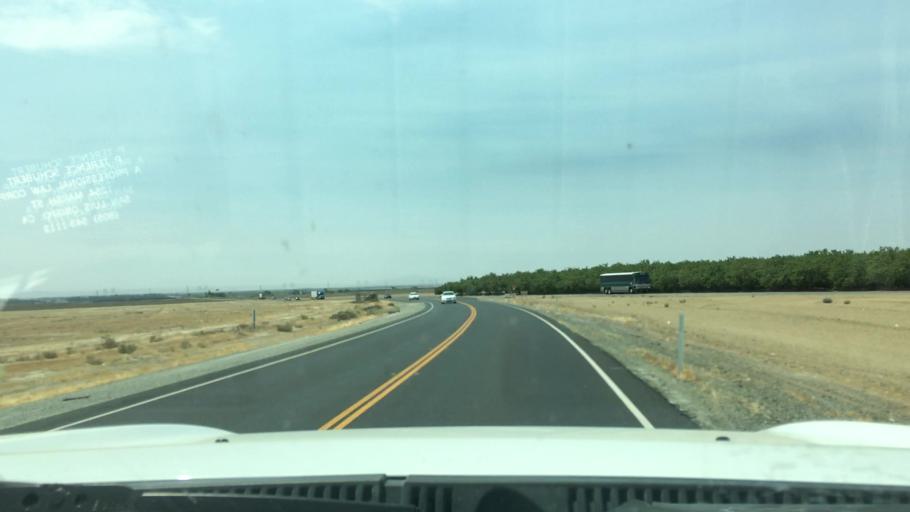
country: US
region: California
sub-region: Kern County
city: Lost Hills
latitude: 35.6152
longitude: -119.5906
